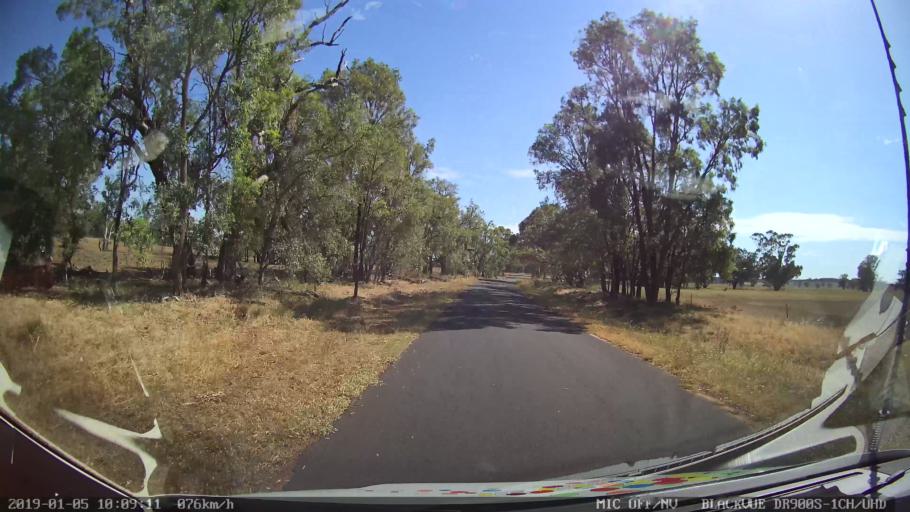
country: AU
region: New South Wales
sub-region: Gilgandra
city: Gilgandra
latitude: -31.6338
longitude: 148.8849
